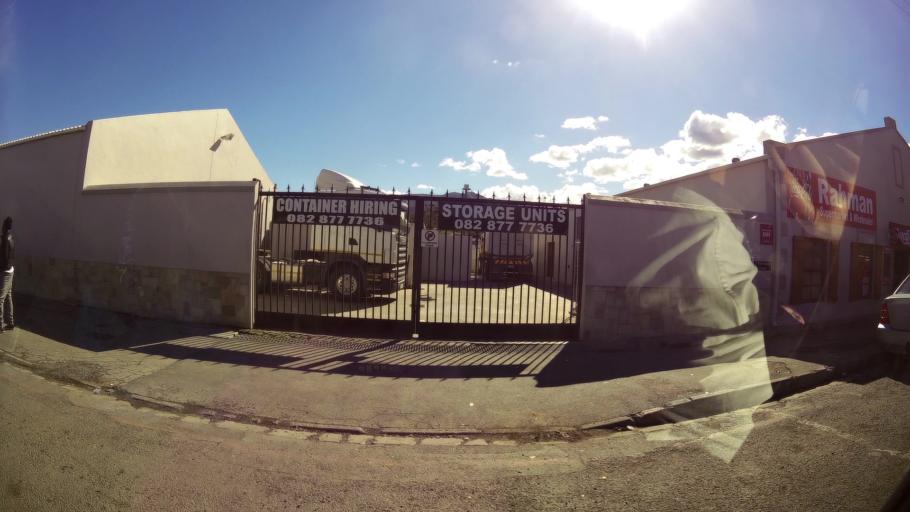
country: ZA
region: Western Cape
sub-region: Cape Winelands District Municipality
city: Ashton
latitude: -33.8059
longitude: 19.8766
